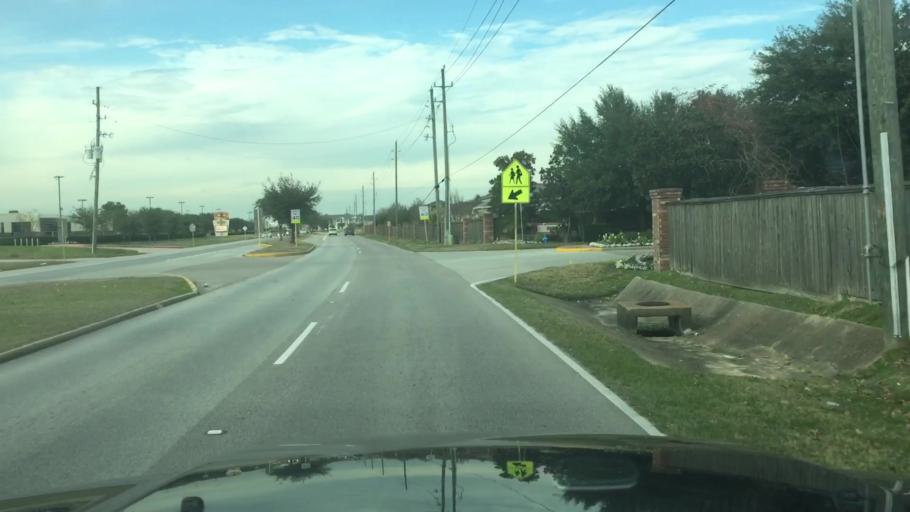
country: US
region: Texas
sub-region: Harris County
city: Oak Cliff Place
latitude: 29.8543
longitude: -95.6683
